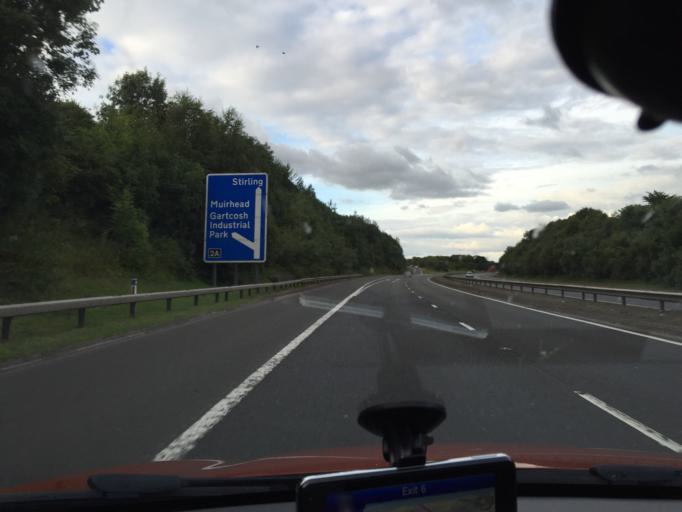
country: GB
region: Scotland
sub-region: North Lanarkshire
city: Chryston
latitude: 55.8863
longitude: -4.0805
